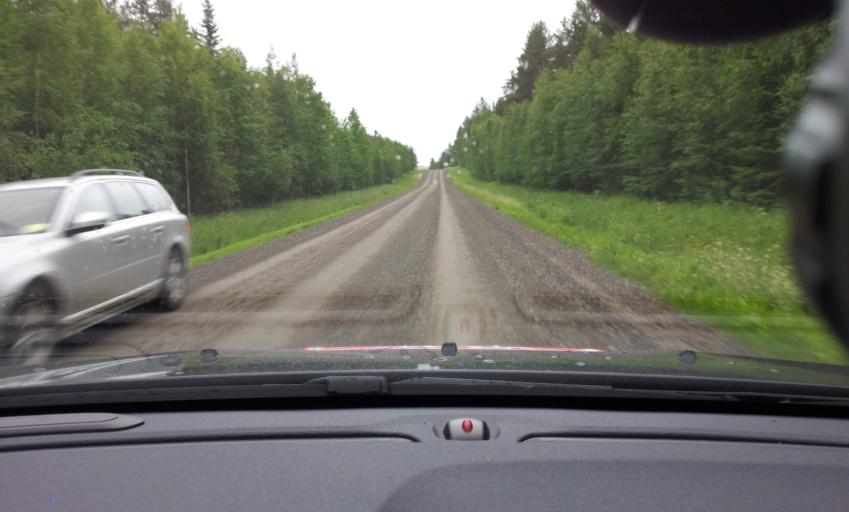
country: SE
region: Jaemtland
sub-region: Ragunda Kommun
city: Hammarstrand
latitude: 63.1204
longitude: 16.3341
